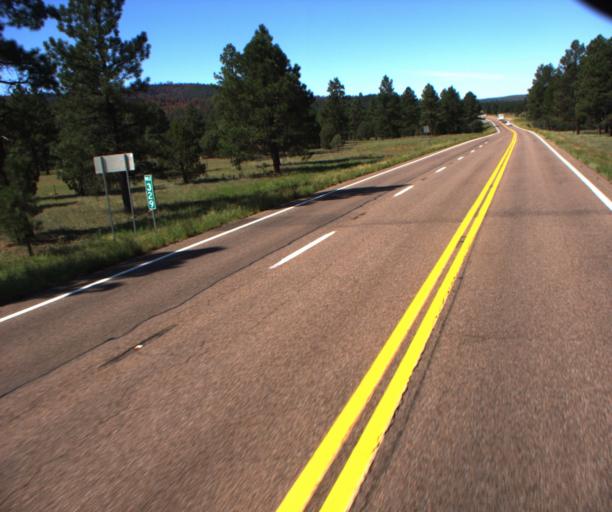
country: US
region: Arizona
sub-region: Navajo County
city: Lake of the Woods
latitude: 34.1126
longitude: -110.1435
